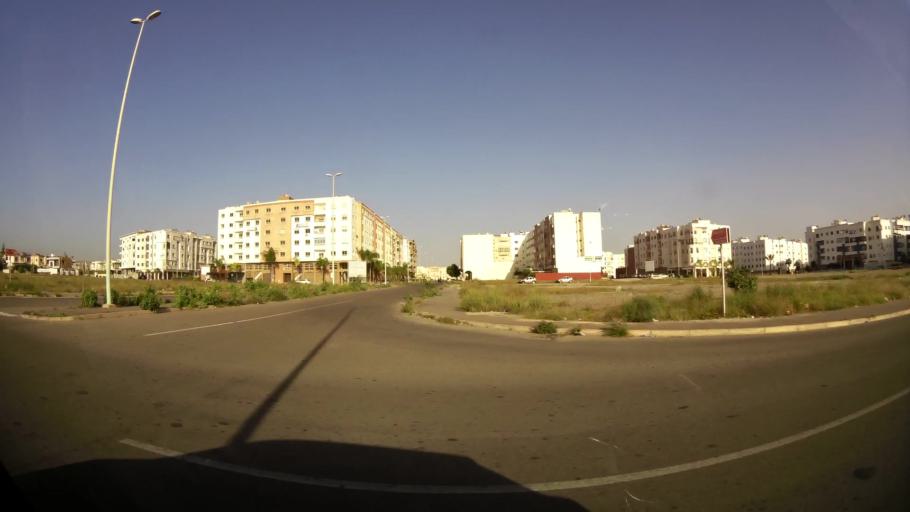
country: MA
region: Oued ed Dahab-Lagouira
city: Dakhla
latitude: 30.3998
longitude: -9.5412
